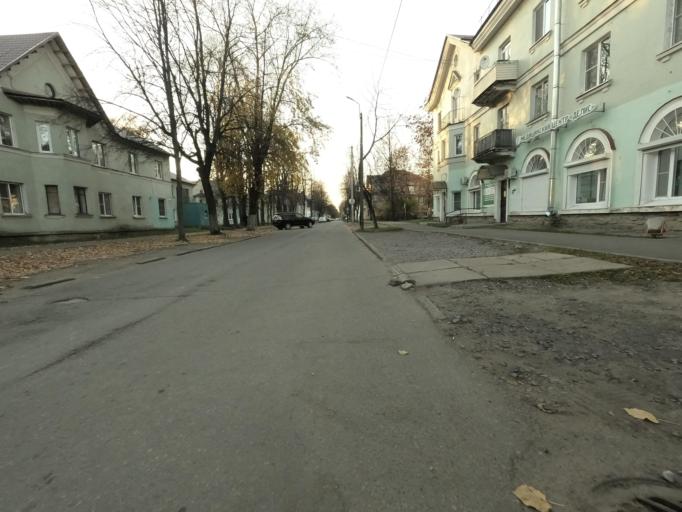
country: RU
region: Leningrad
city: Kirovsk
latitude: 59.8727
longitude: 30.9936
